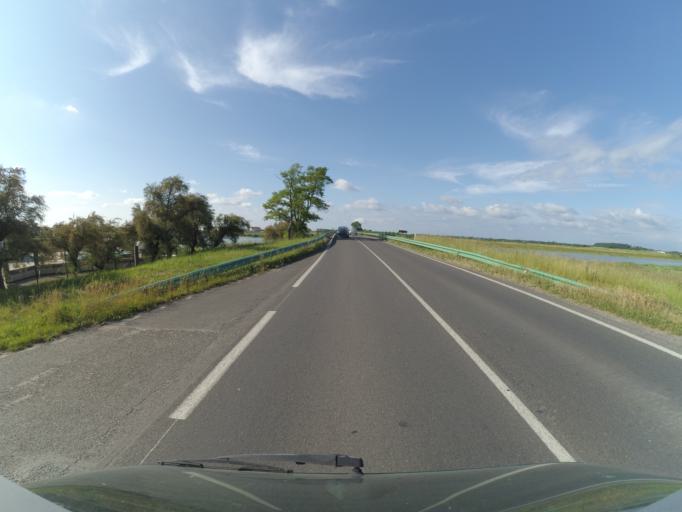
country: FR
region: Poitou-Charentes
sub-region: Departement de la Charente-Maritime
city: Le Gua
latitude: 45.7082
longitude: -0.9727
